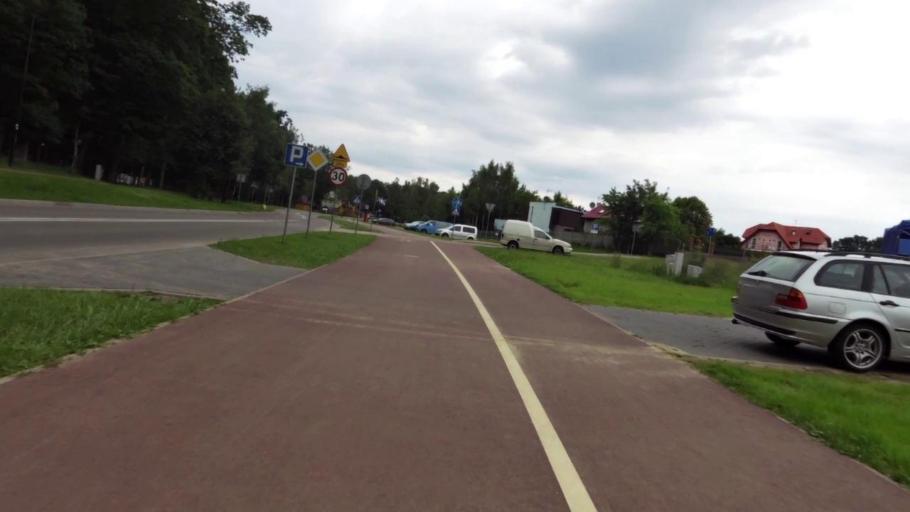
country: PL
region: West Pomeranian Voivodeship
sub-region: Powiat gryficki
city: Rewal
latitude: 54.0847
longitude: 15.0346
